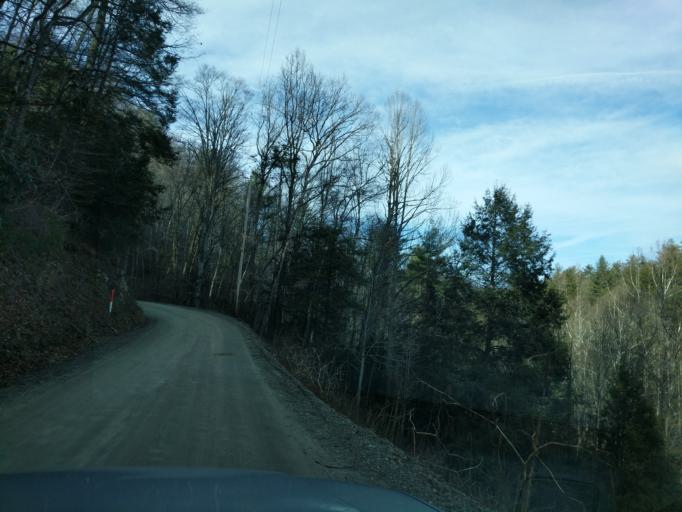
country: US
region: North Carolina
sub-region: Haywood County
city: Cove Creek
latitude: 35.6675
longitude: -83.0228
